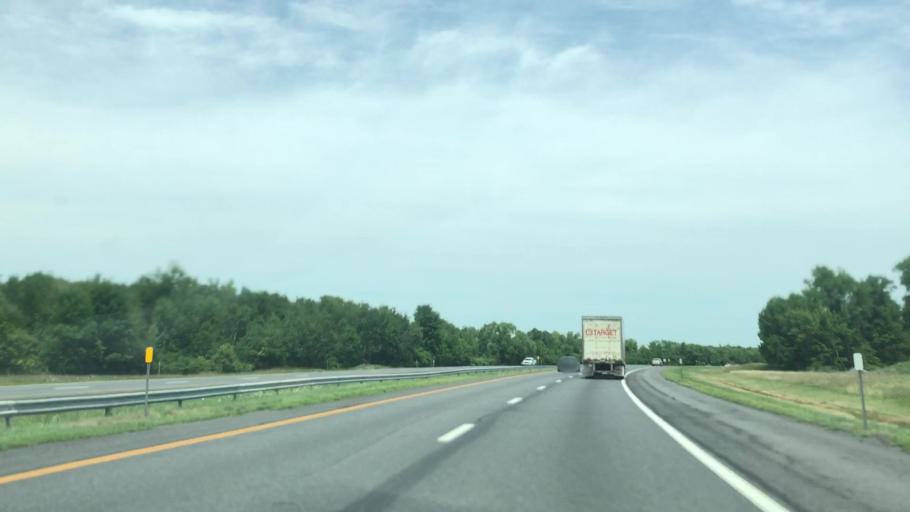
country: US
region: New York
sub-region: Albany County
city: Ravena
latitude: 42.4820
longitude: -73.8082
